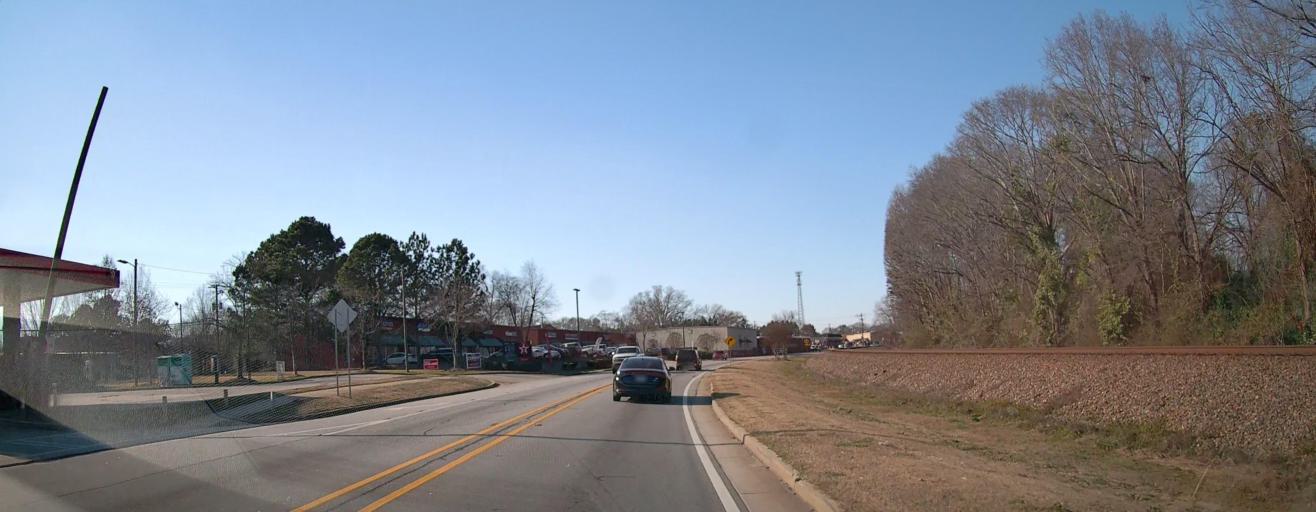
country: US
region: Georgia
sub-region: Henry County
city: Locust Grove
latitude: 33.3438
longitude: -84.1076
